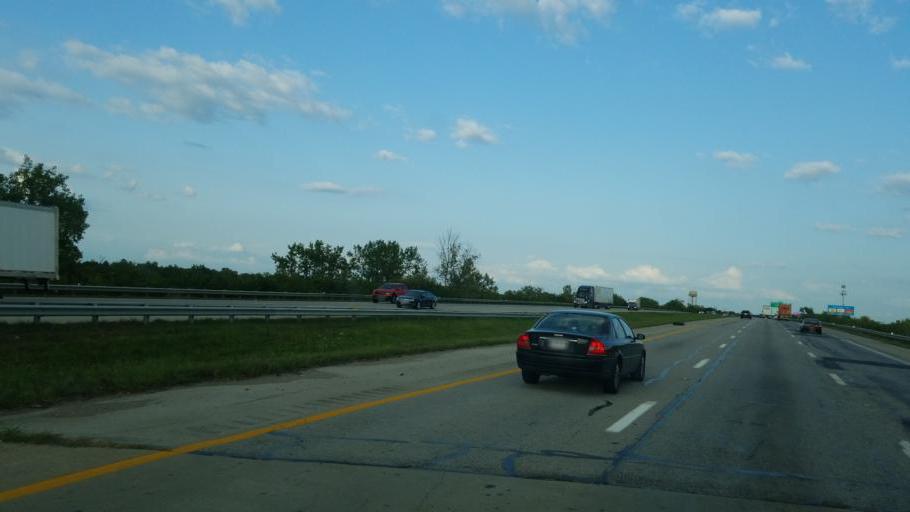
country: US
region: Ohio
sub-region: Franklin County
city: Obetz
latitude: 39.8721
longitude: -82.9593
